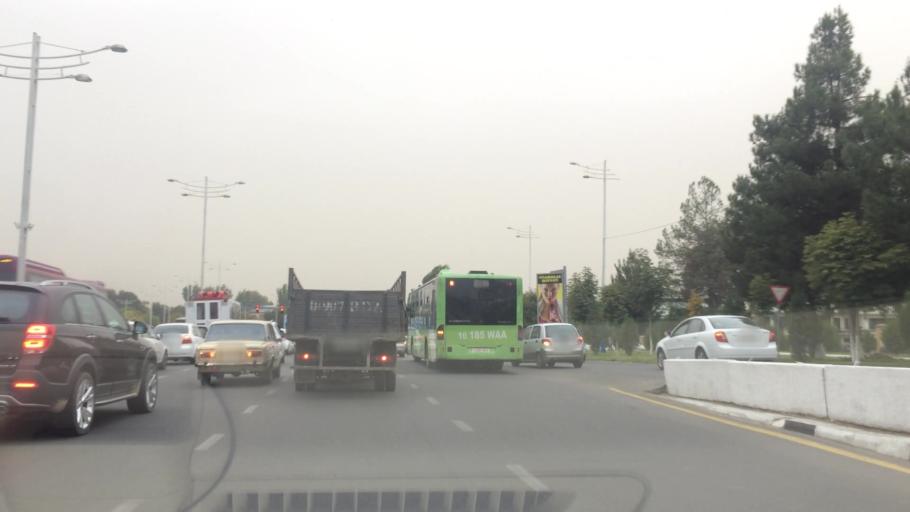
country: UZ
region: Toshkent Shahri
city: Tashkent
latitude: 41.3076
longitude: 69.3012
